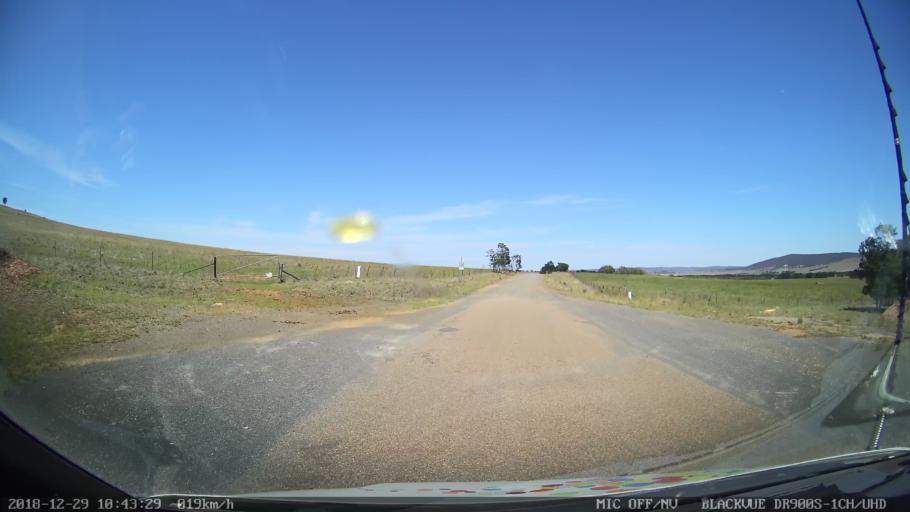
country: AU
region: New South Wales
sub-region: Palerang
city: Bungendore
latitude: -35.0406
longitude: 149.5368
